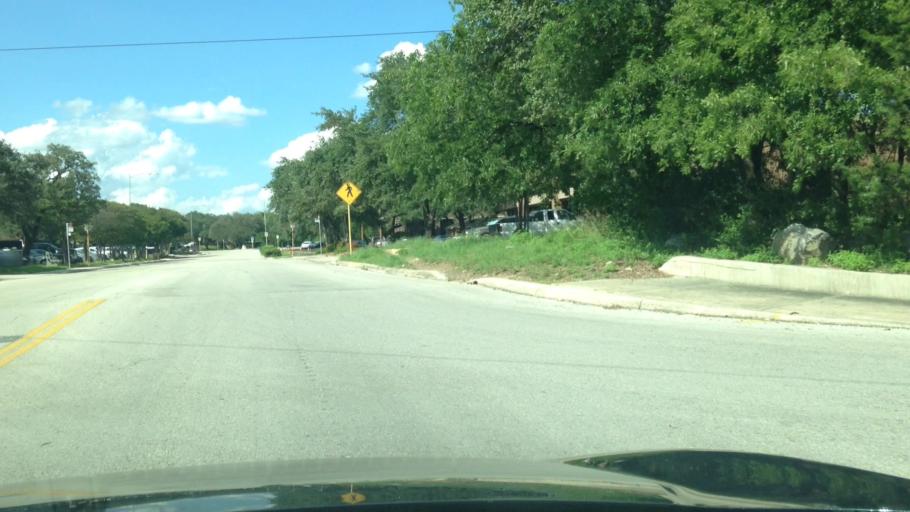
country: US
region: Texas
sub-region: Bexar County
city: Shavano Park
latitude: 29.5437
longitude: -98.5864
